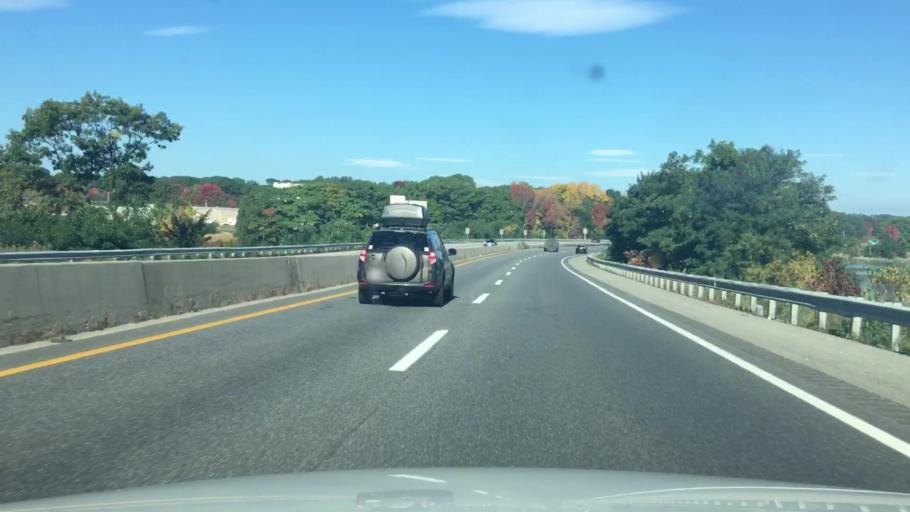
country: US
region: Maine
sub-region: Cumberland County
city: Portland
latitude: 43.6876
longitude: -70.2537
